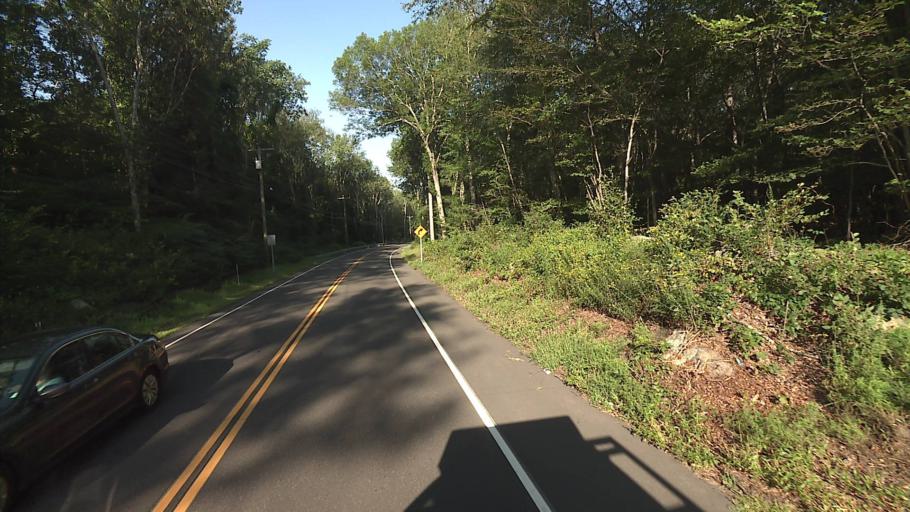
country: US
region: Connecticut
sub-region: New London County
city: Niantic
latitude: 41.3490
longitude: -72.2784
